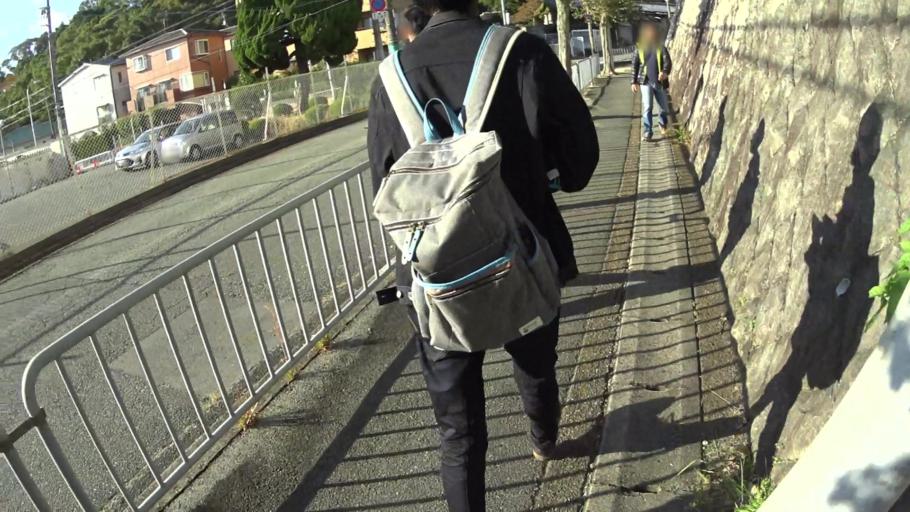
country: JP
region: Osaka
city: Ikeda
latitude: 34.8284
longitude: 135.4323
